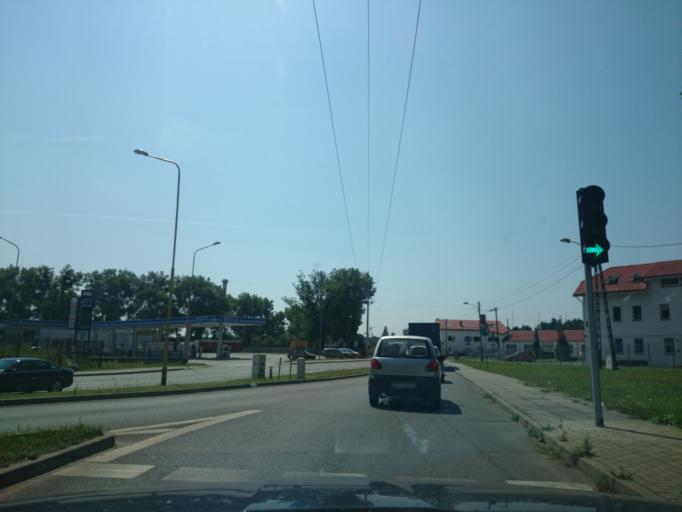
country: PL
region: West Pomeranian Voivodeship
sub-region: Powiat gryfinski
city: Stare Czarnowo
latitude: 53.3641
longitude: 14.7344
